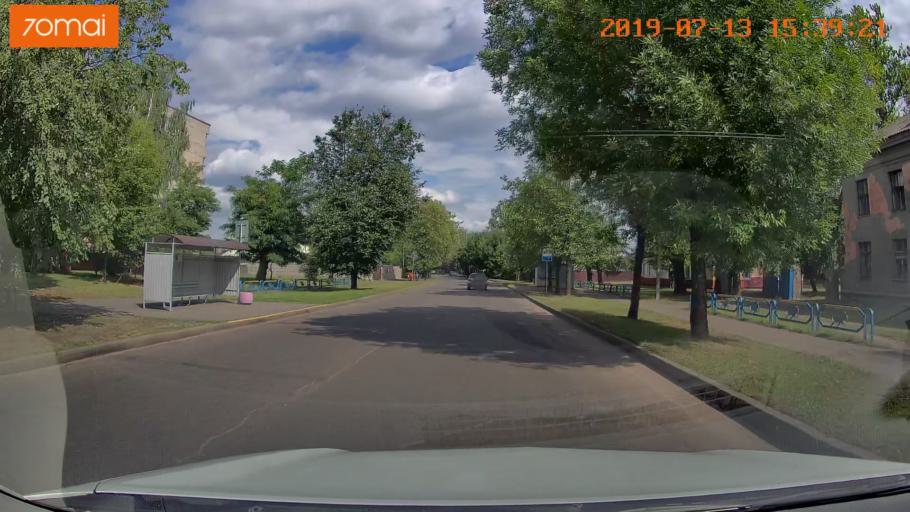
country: BY
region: Mogilev
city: Babruysk
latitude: 53.1354
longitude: 29.1798
